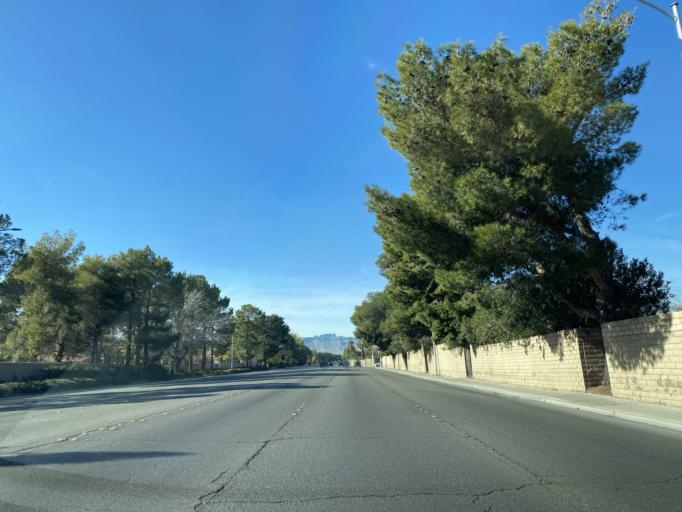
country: US
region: Nevada
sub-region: Clark County
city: Spring Valley
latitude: 36.0998
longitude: -115.2506
